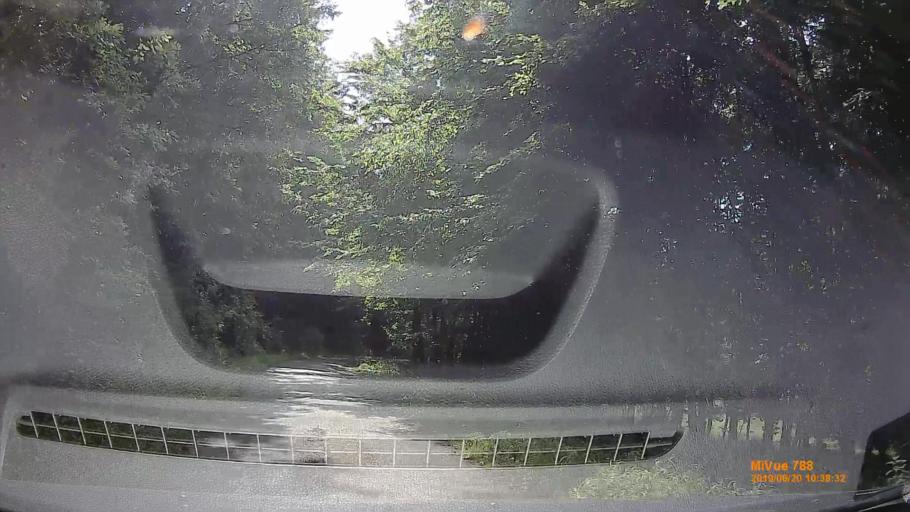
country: HU
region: Baranya
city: Hidas
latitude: 46.1998
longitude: 18.5373
